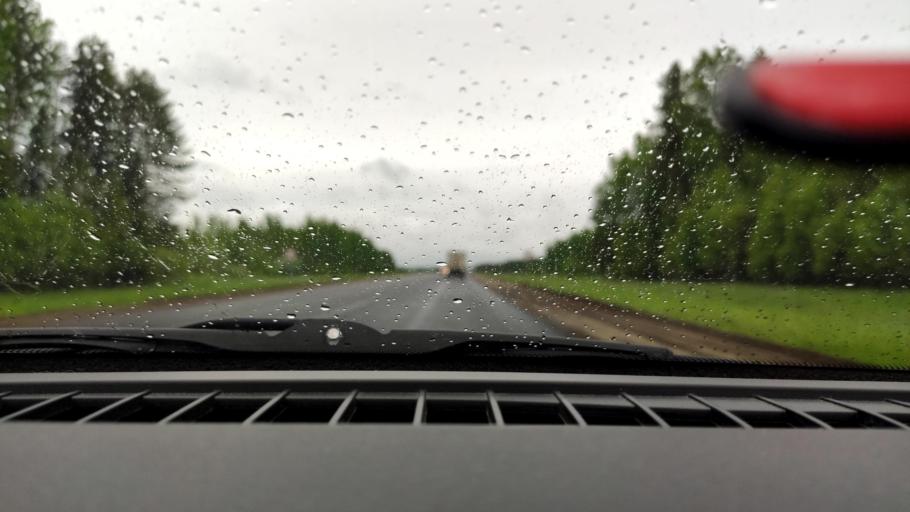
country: RU
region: Perm
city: Karagay
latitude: 58.2472
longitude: 54.9307
